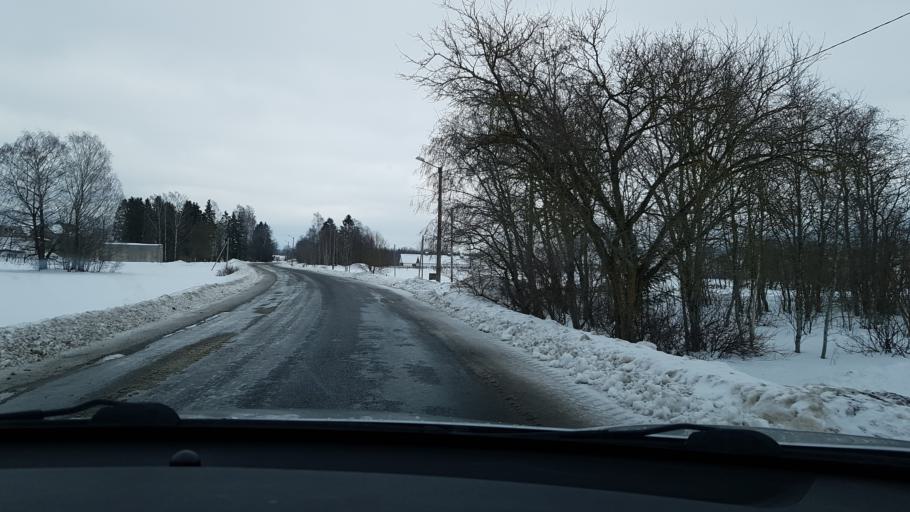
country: EE
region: Jaervamaa
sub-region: Koeru vald
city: Koeru
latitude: 58.9721
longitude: 26.0092
